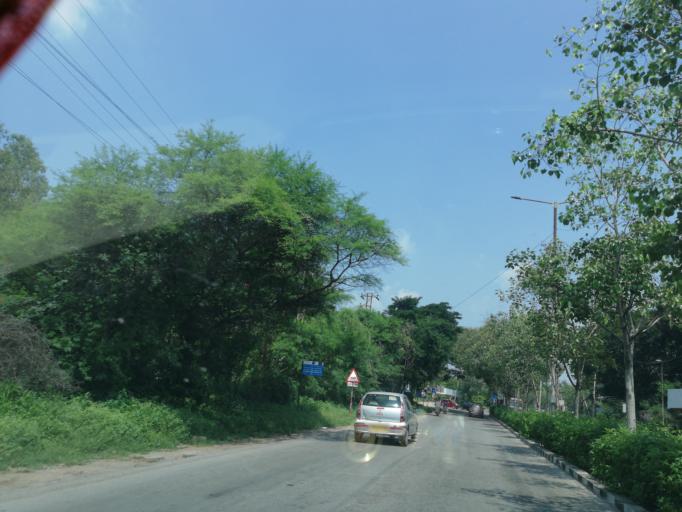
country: IN
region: Telangana
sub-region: Medak
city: Serilingampalle
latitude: 17.4612
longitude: 78.3364
